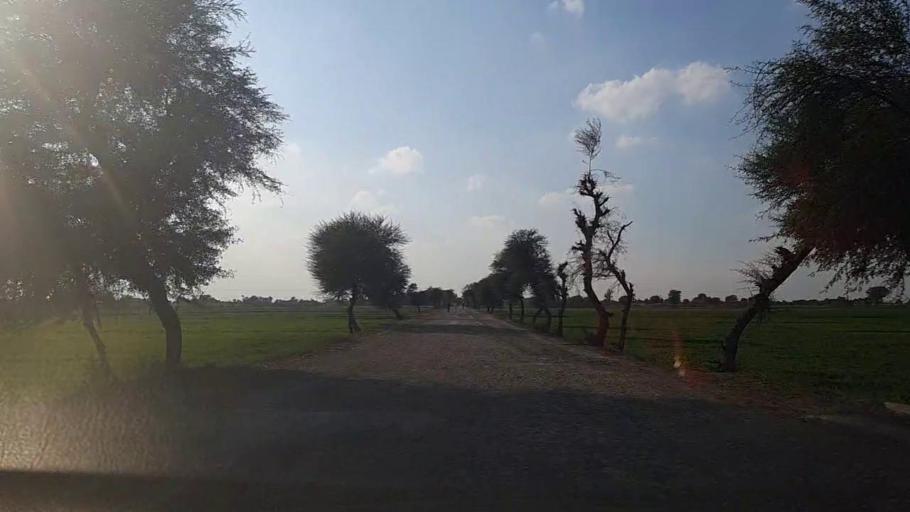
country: PK
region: Sindh
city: Jhol
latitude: 25.8381
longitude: 69.0598
